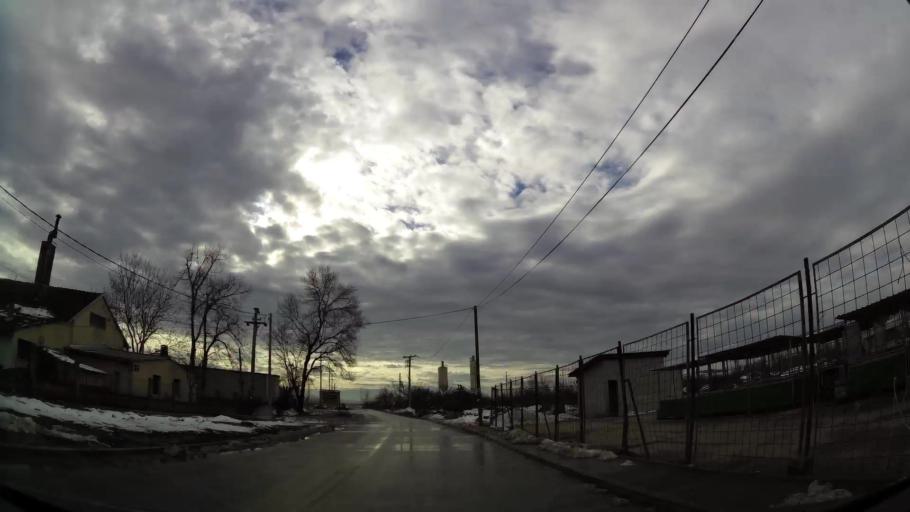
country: RS
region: Central Serbia
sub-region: Belgrade
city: Surcin
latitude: 44.7885
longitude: 20.2709
